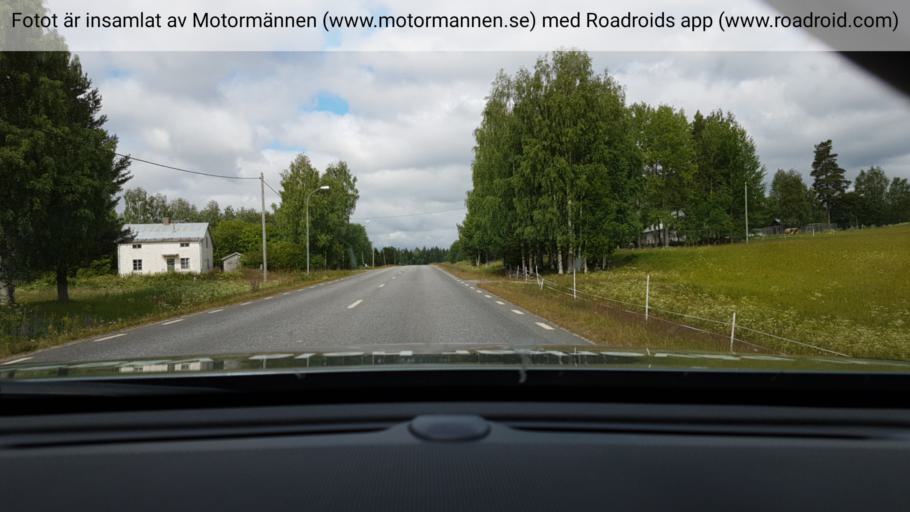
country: SE
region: Vaesterbotten
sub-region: Mala Kommun
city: Mala
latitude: 64.9888
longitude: 18.5029
